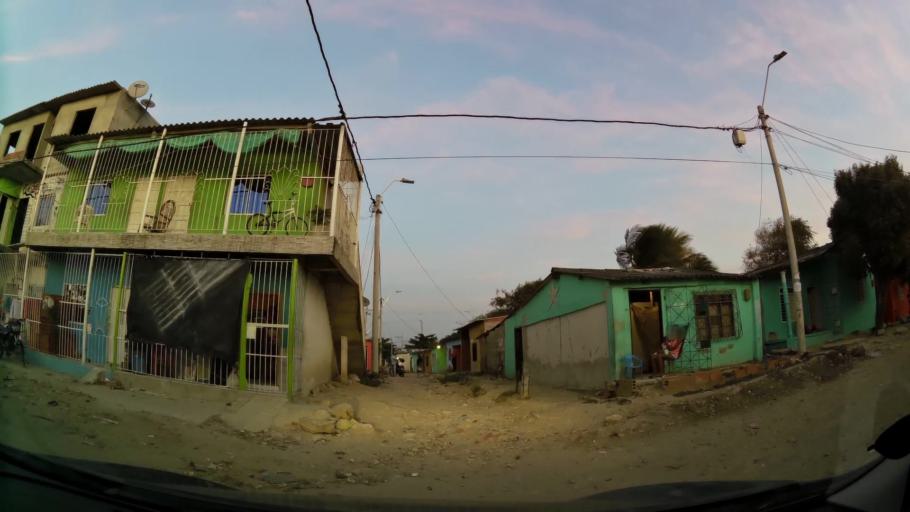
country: CO
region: Atlantico
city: Barranquilla
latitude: 10.9525
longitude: -74.8278
